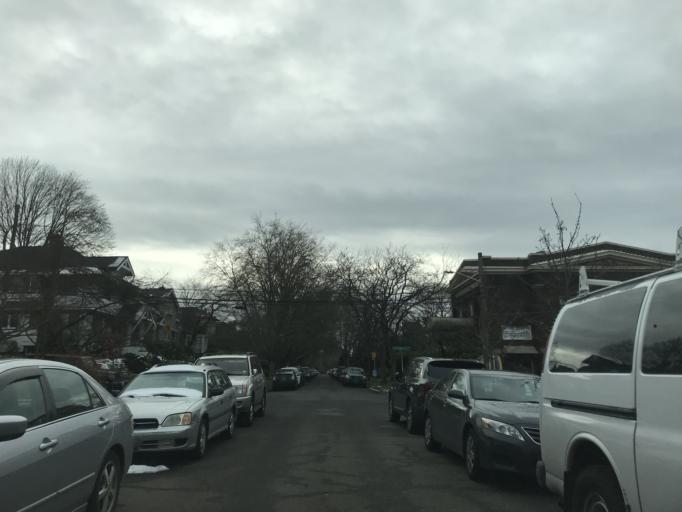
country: US
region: Washington
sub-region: King County
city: Seattle
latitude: 47.6290
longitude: -122.3061
